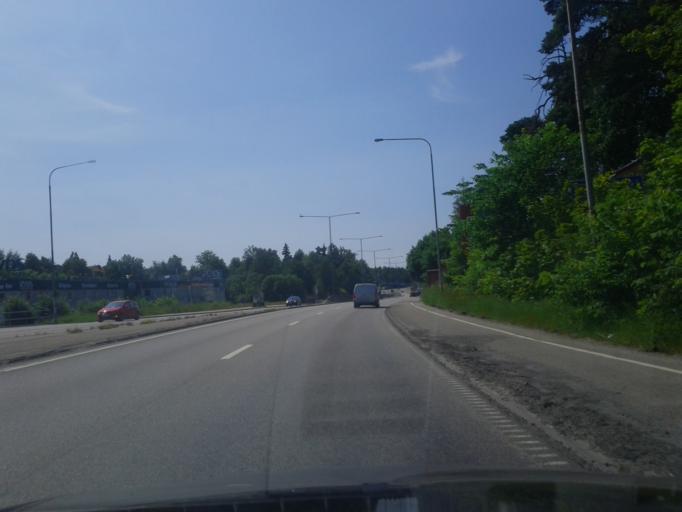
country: SE
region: Stockholm
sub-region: Huddinge Kommun
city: Huddinge
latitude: 59.2553
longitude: 18.0138
